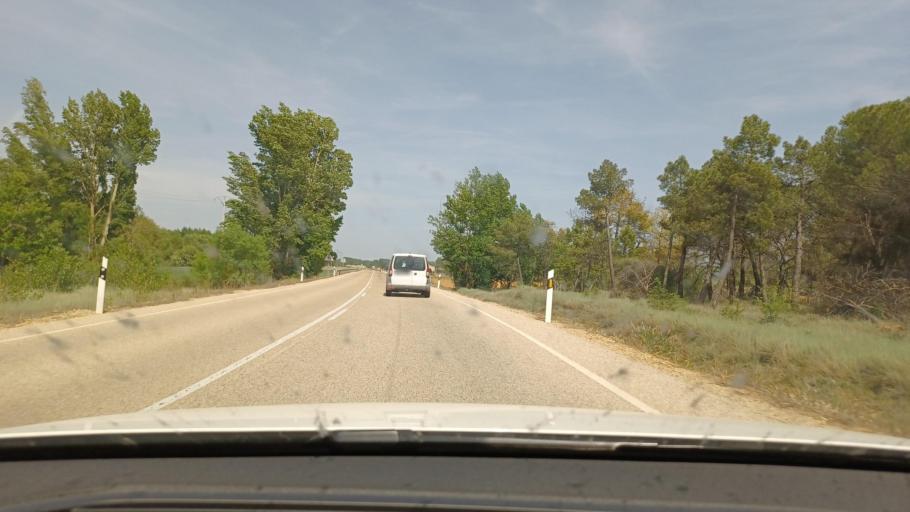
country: ES
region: Castille and Leon
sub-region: Provincia de Soria
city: Barca
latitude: 41.4695
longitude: -2.5820
